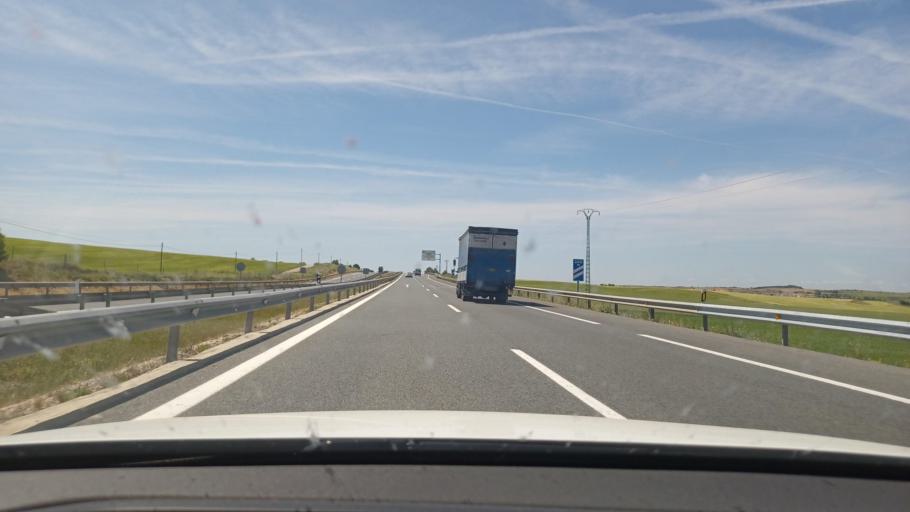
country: ES
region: Castille-La Mancha
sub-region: Provincia de Cuenca
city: Villarrubio
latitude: 39.9412
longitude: -2.8757
